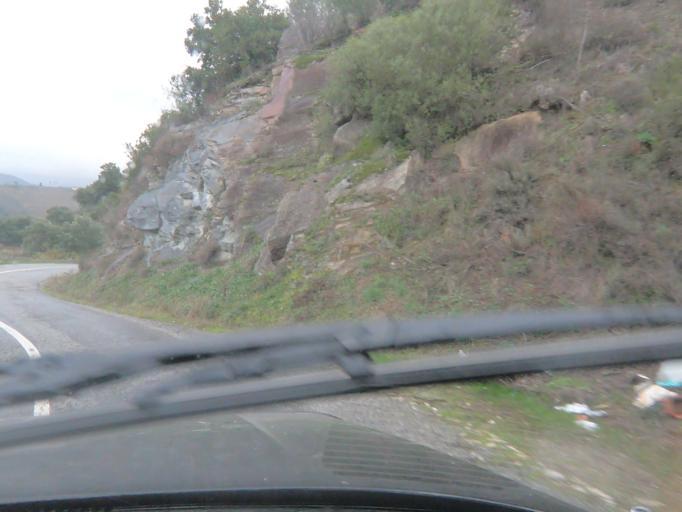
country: PT
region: Vila Real
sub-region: Santa Marta de Penaguiao
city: Santa Marta de Penaguiao
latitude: 41.2125
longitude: -7.7537
